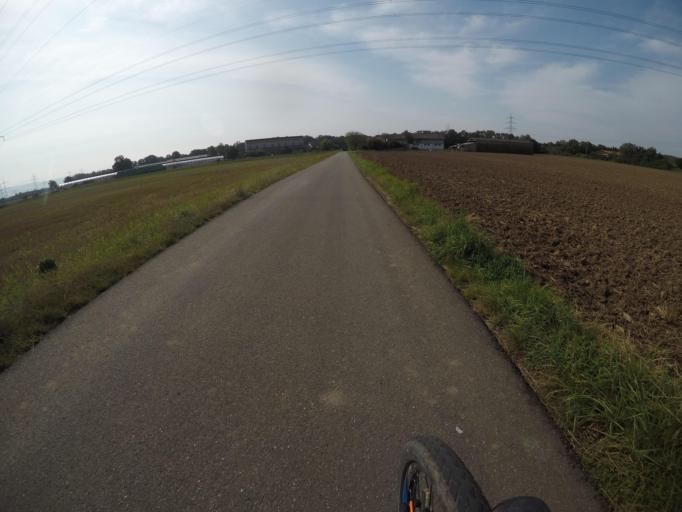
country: DE
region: Baden-Wuerttemberg
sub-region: Karlsruhe Region
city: Plankstadt
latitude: 49.4275
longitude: 8.5716
